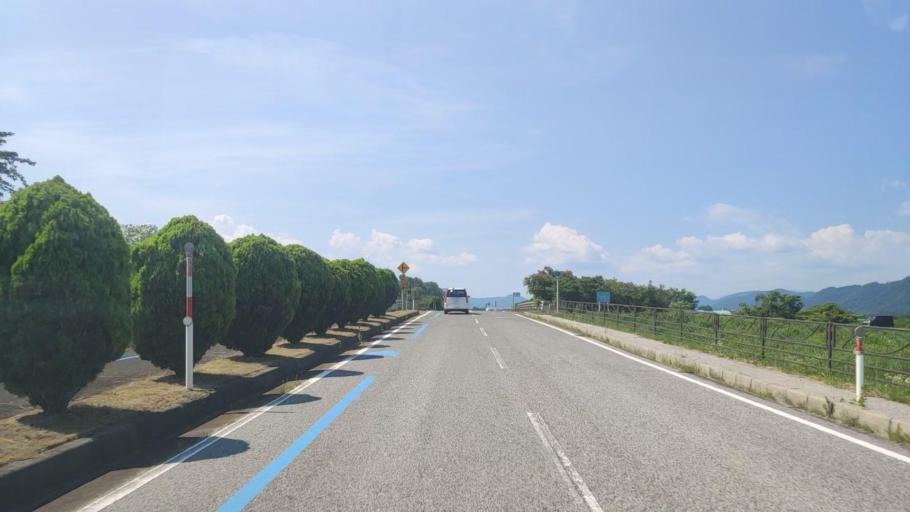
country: JP
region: Shiga Prefecture
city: Nagahama
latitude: 35.4194
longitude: 136.2004
